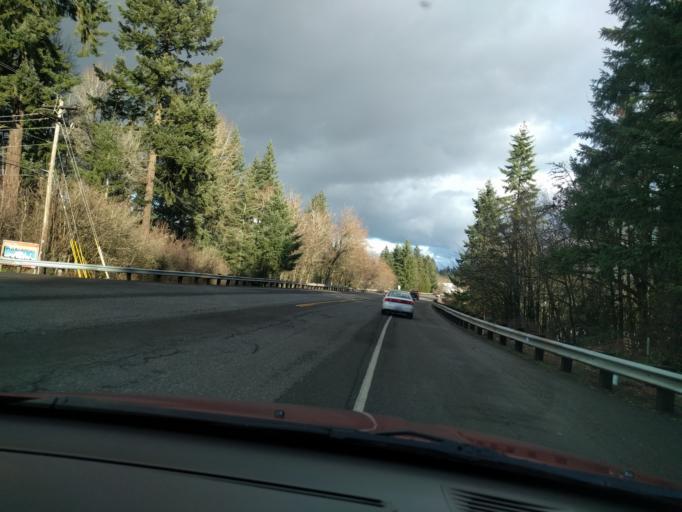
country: US
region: Oregon
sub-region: Clackamas County
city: Damascus
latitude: 45.4272
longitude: -122.3830
